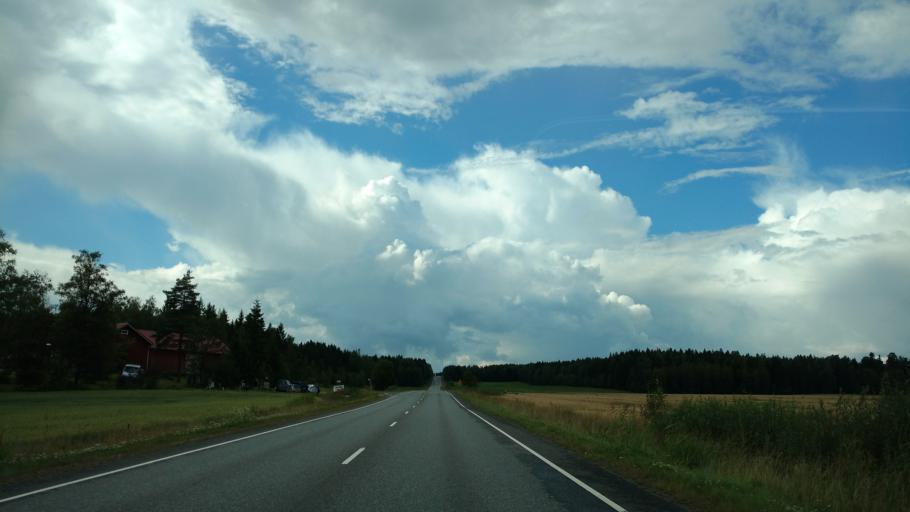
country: FI
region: Varsinais-Suomi
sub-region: Turku
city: Sauvo
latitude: 60.3965
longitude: 22.8492
